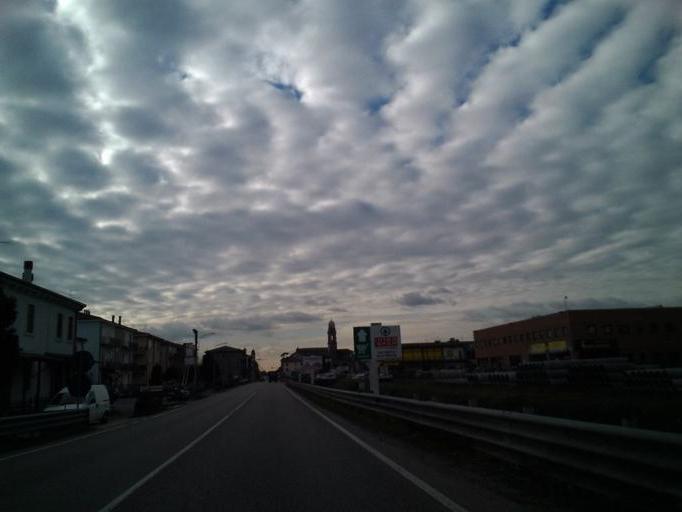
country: IT
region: Veneto
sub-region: Provincia di Verona
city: Monticelli-Fontana
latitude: 45.4189
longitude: 11.1424
